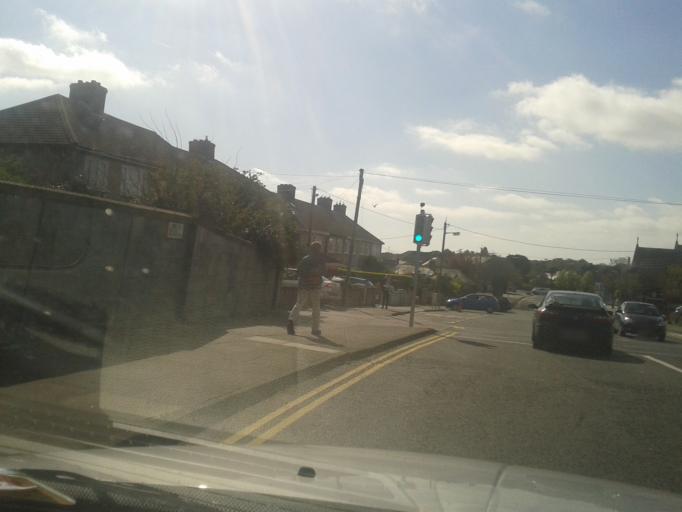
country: IE
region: Leinster
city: Raheny
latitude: 53.3816
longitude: -6.1759
